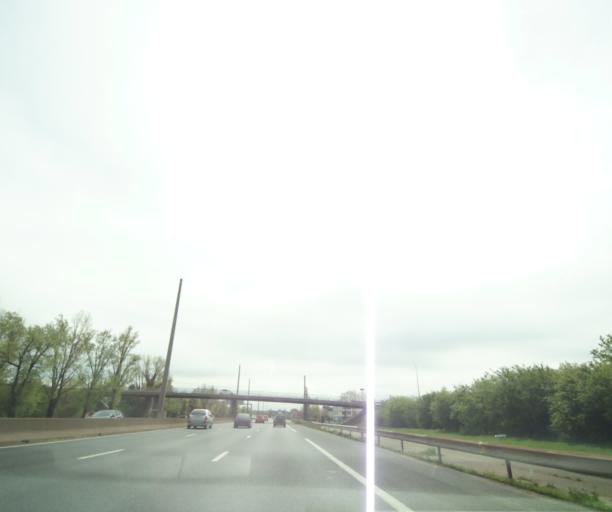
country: FR
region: Rhone-Alpes
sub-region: Departement du Rhone
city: Pierre-Benite
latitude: 45.7074
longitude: 4.8307
